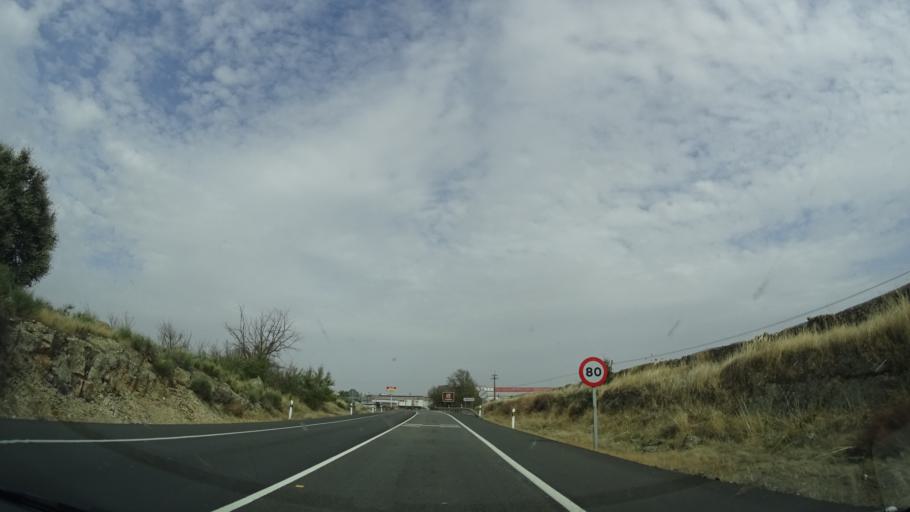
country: ES
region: Extremadura
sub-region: Provincia de Caceres
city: Trujillo
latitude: 39.4468
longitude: -5.8821
